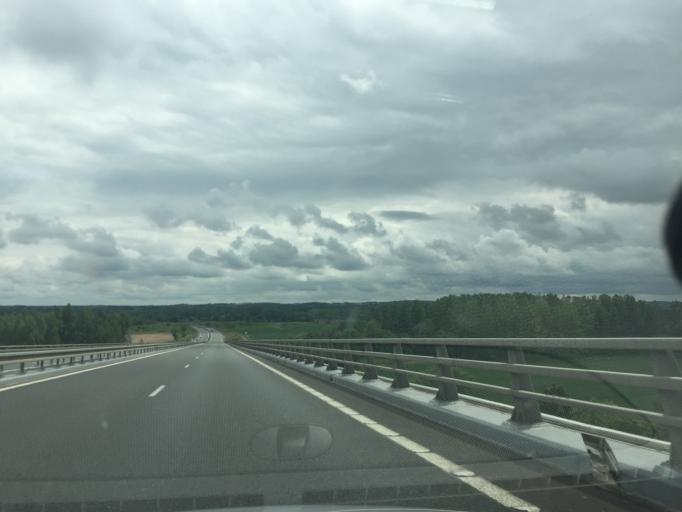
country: FR
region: Pays de la Loire
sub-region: Departement de la Sarthe
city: Luceau
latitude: 47.6772
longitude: 0.3711
